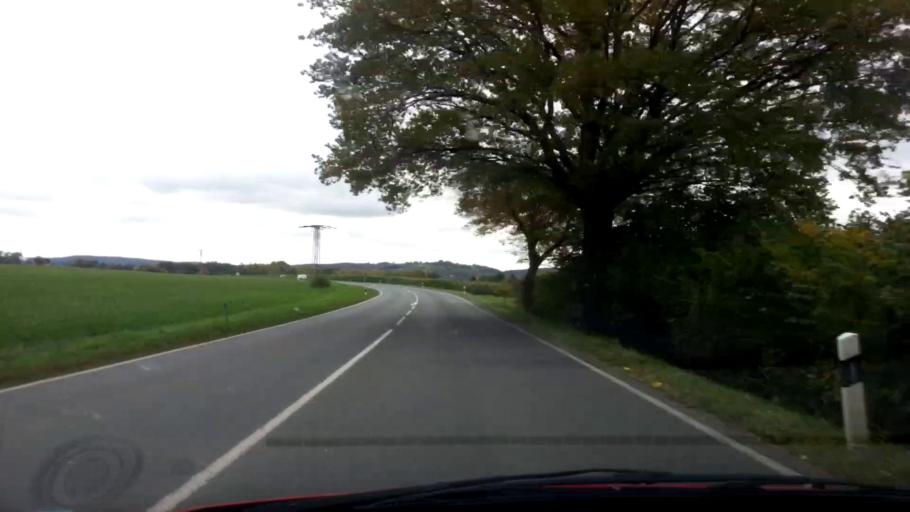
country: DE
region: Bavaria
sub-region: Upper Franconia
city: Reuth
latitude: 49.9542
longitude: 11.7053
